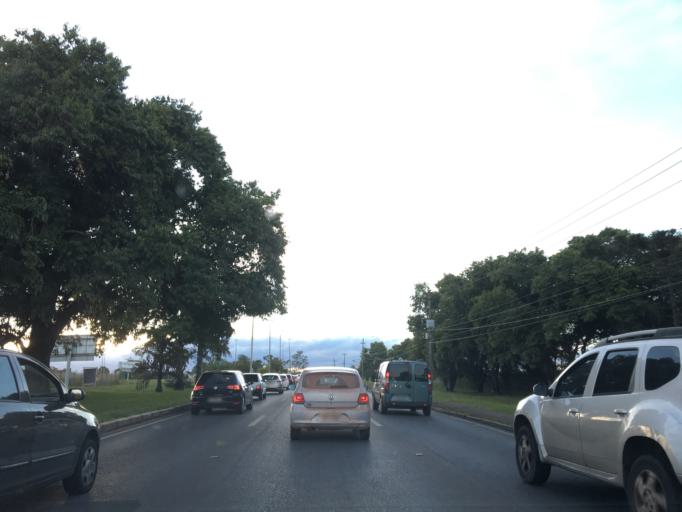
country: BR
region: Federal District
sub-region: Brasilia
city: Brasilia
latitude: -15.8372
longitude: -47.9638
